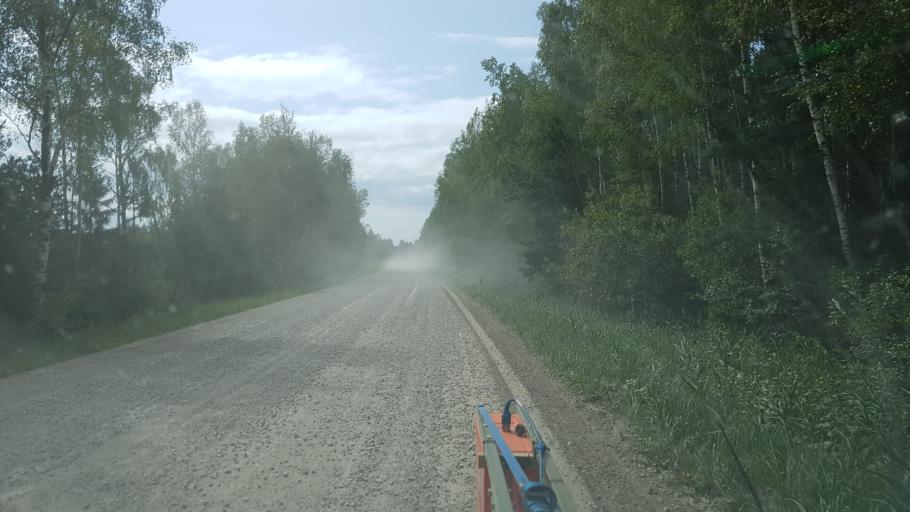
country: EE
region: Paernumaa
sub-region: Audru vald
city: Audru
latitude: 58.5199
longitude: 24.4052
